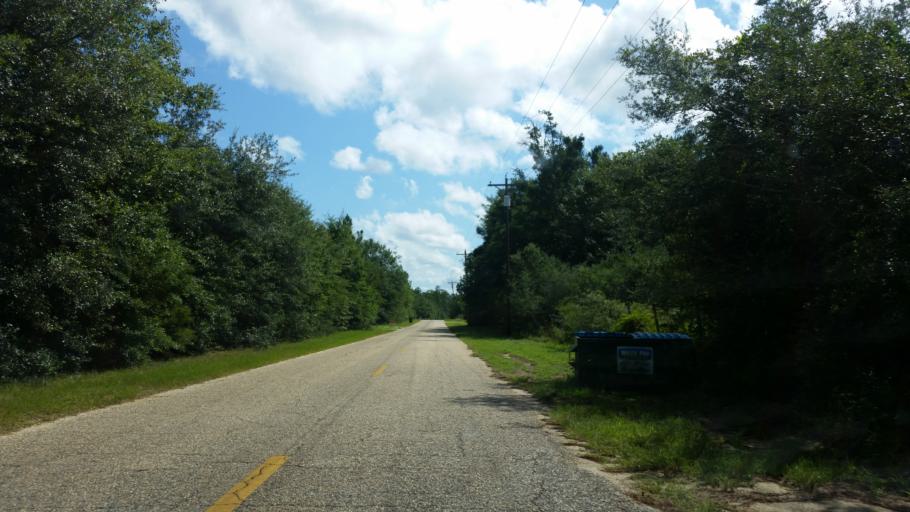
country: US
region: Florida
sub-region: Santa Rosa County
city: Point Baker
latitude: 30.7240
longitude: -86.9090
